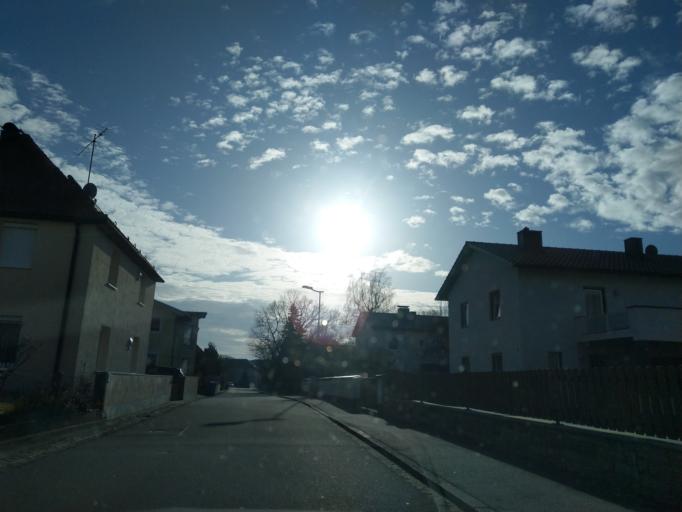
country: DE
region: Bavaria
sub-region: Lower Bavaria
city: Osterhofen
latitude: 48.7055
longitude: 13.0175
